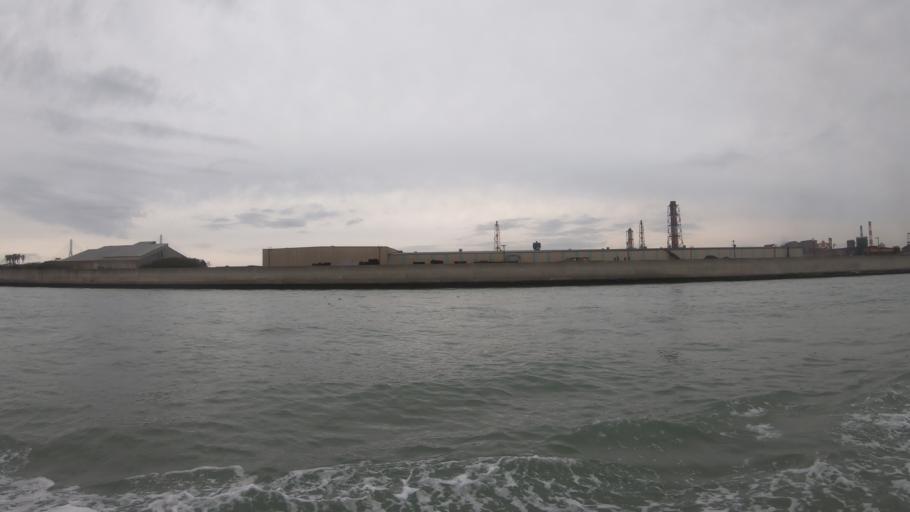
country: JP
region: Kanagawa
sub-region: Kawasaki-shi
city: Kawasaki
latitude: 35.4663
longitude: 139.7209
